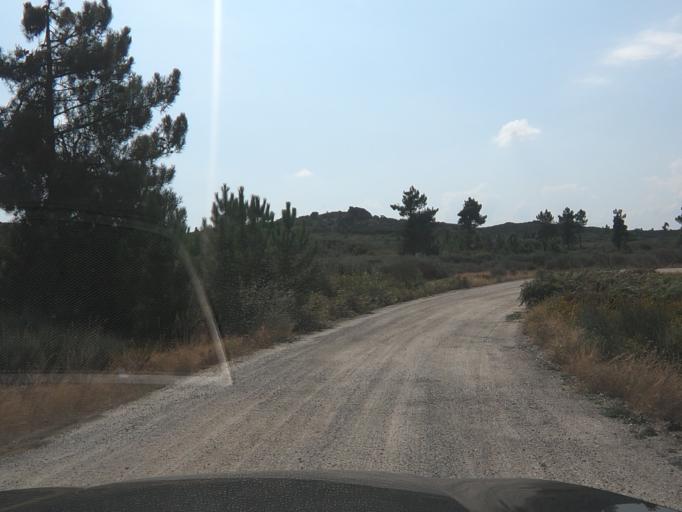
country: PT
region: Vila Real
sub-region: Sabrosa
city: Sabrosa
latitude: 41.3127
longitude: -7.6228
